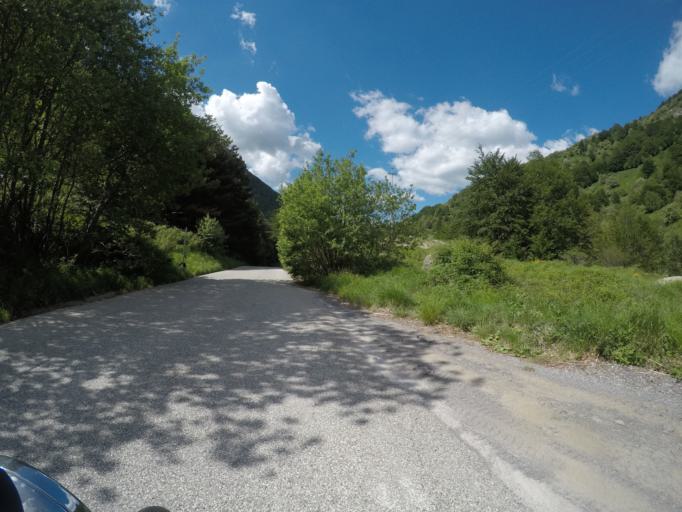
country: IT
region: Tuscany
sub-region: Provincia di Lucca
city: Minucciano
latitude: 44.1380
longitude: 10.1964
